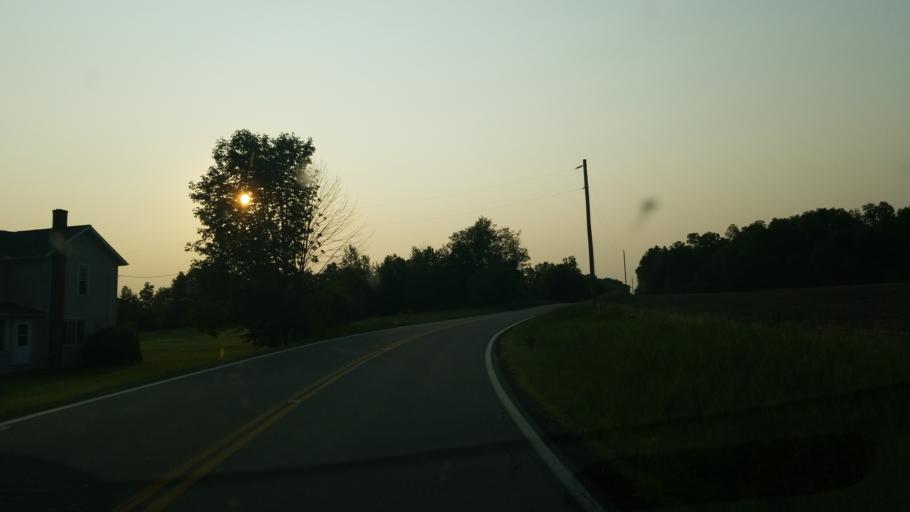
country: US
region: Ohio
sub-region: Ashland County
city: Ashland
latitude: 40.9379
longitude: -82.3177
